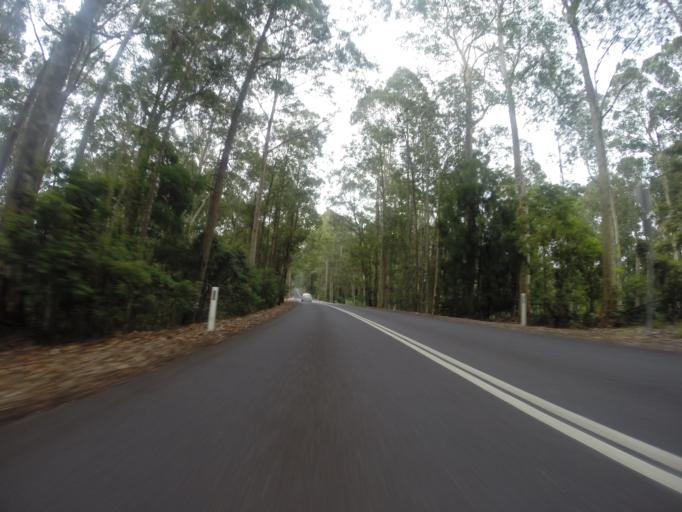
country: AU
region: New South Wales
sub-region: Eurobodalla
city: Batemans Bay
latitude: -35.6557
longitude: 150.2512
